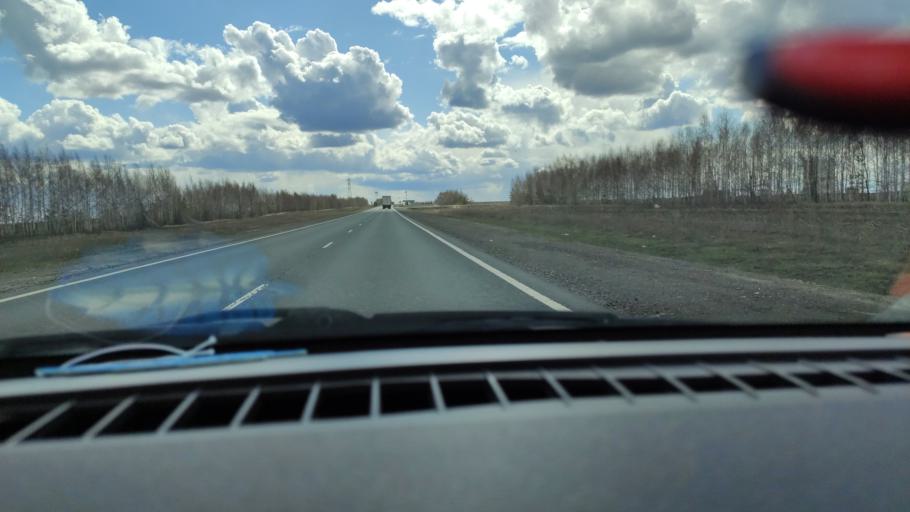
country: RU
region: Saratov
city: Dukhovnitskoye
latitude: 52.8417
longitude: 48.2481
